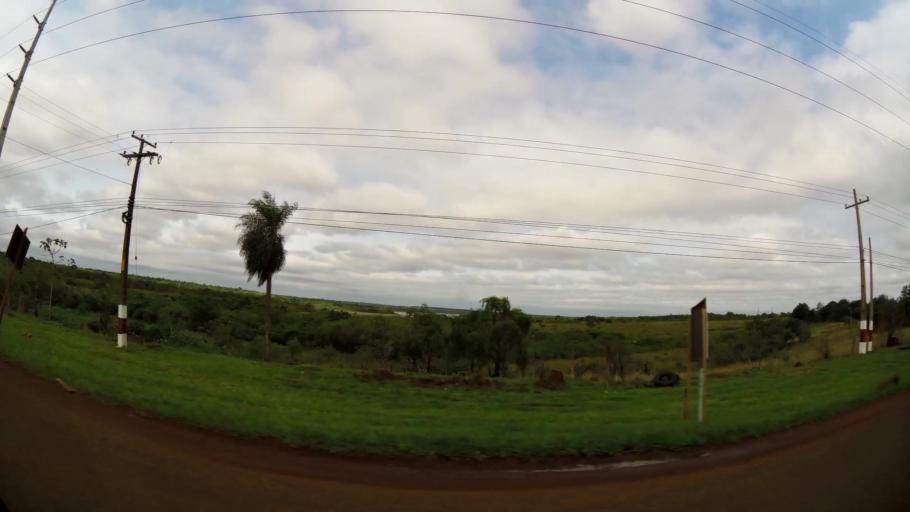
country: PY
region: Alto Parana
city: Ciudad del Este
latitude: -25.3812
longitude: -54.6431
